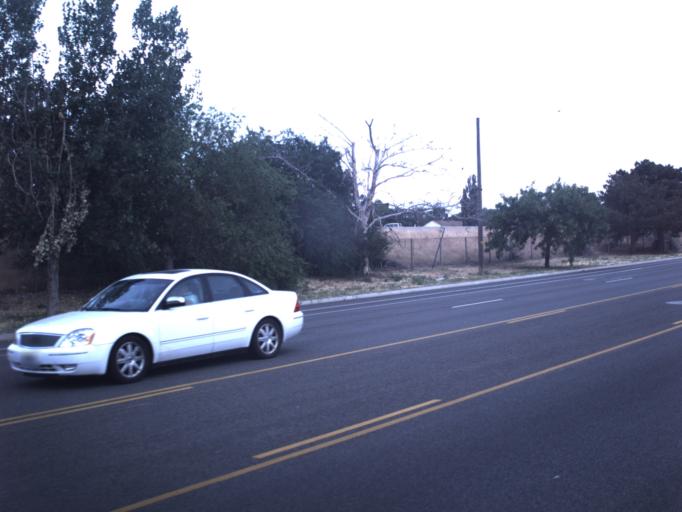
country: US
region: Utah
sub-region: Davis County
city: Sunset
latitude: 41.1384
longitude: -112.0262
